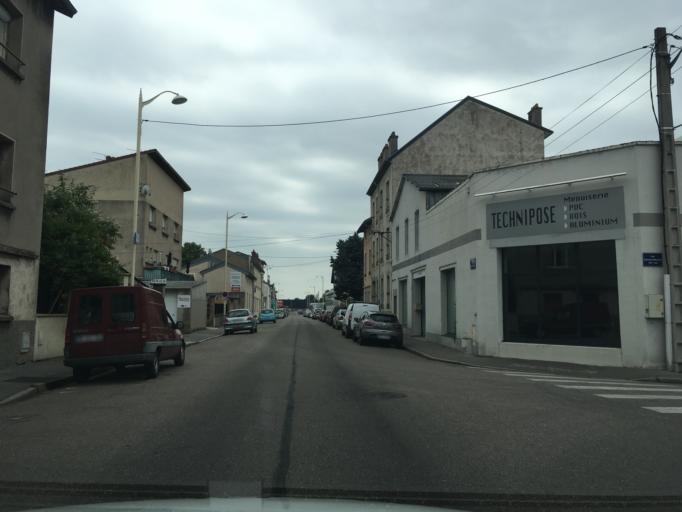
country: FR
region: Lorraine
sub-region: Departement de Meurthe-et-Moselle
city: Tomblaine
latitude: 48.6856
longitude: 6.2000
